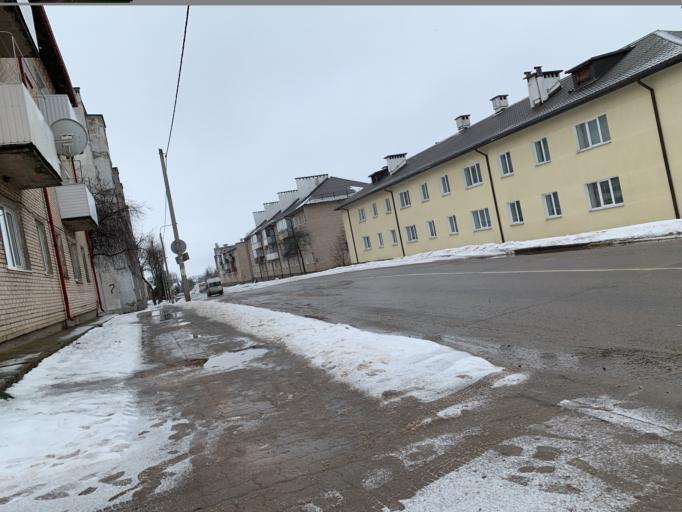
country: BY
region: Minsk
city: Nyasvizh
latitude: 53.2197
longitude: 26.6793
